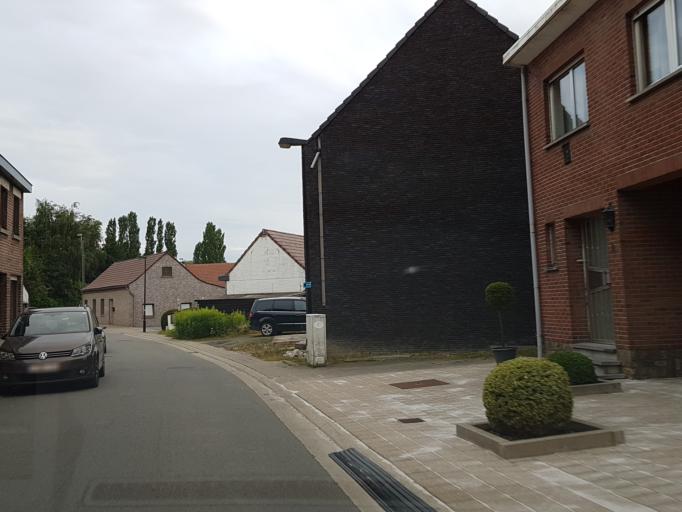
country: BE
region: Flanders
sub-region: Provincie Vlaams-Brabant
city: Asse
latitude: 50.9034
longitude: 4.1660
